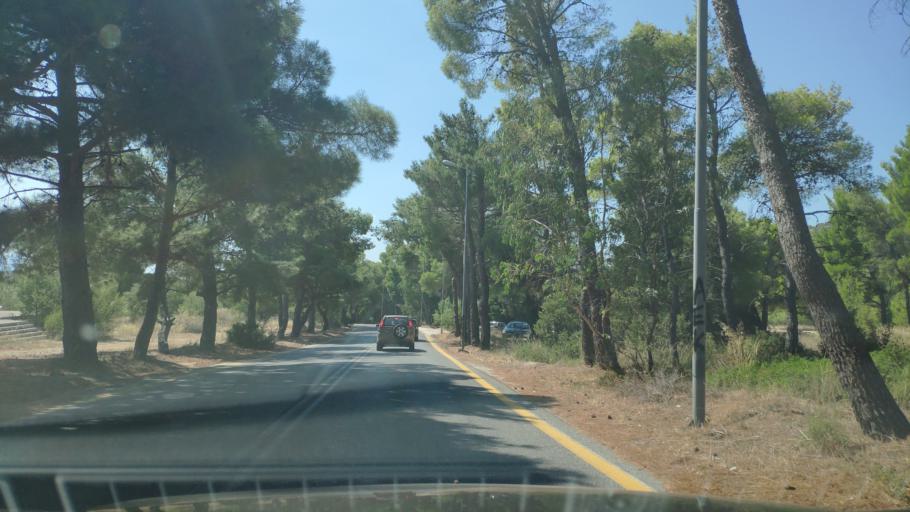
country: GR
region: Attica
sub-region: Nomarchia Anatolikis Attikis
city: Thrakomakedones
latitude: 38.1276
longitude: 23.7327
